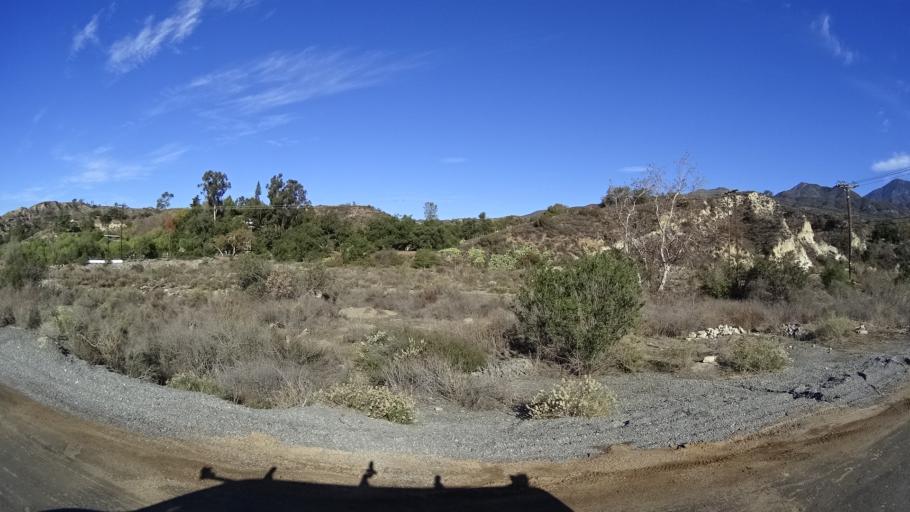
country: US
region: California
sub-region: Orange County
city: Trabuco Canyon
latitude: 33.6597
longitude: -117.5838
